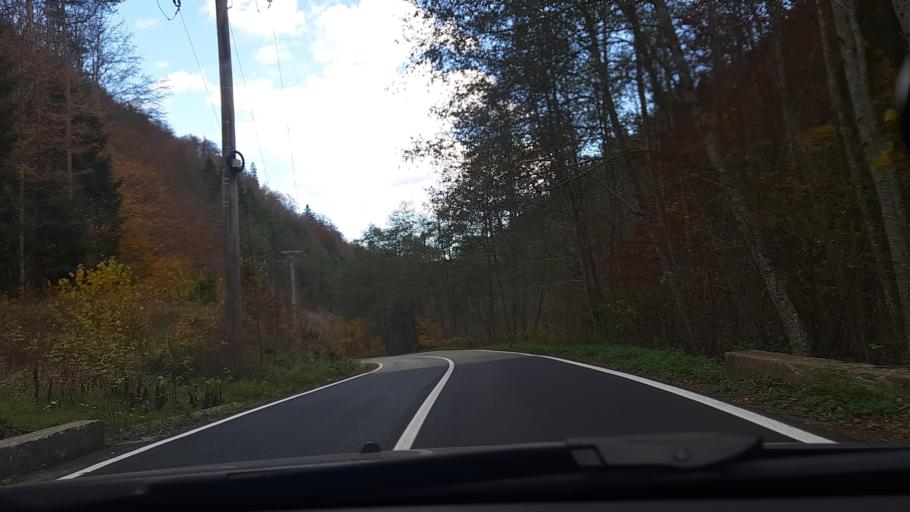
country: RO
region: Valcea
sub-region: Comuna Voineasa
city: Voineasa
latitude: 45.4318
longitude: 23.8954
